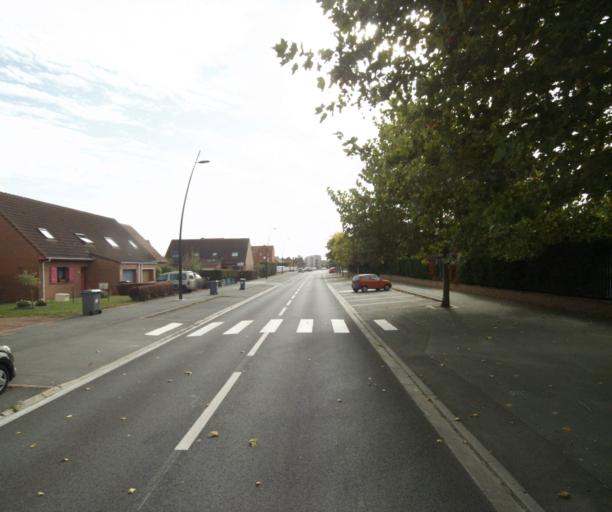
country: FR
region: Nord-Pas-de-Calais
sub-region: Departement du Nord
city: La Bassee
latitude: 50.5375
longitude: 2.8115
